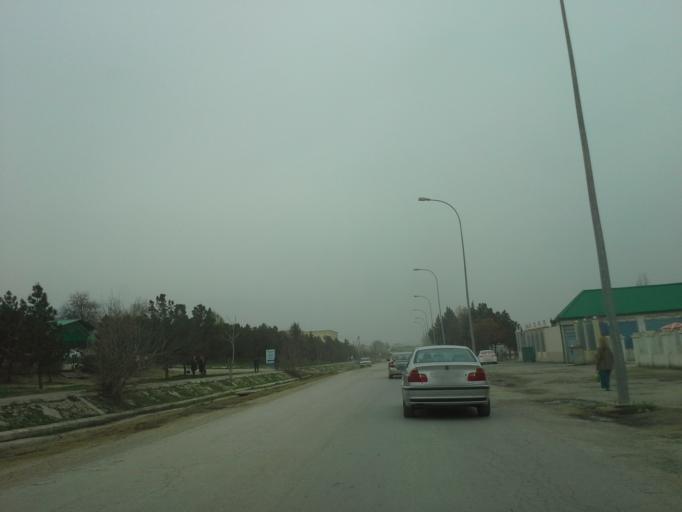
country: TM
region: Ahal
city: Abadan
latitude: 37.9660
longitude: 58.2191
